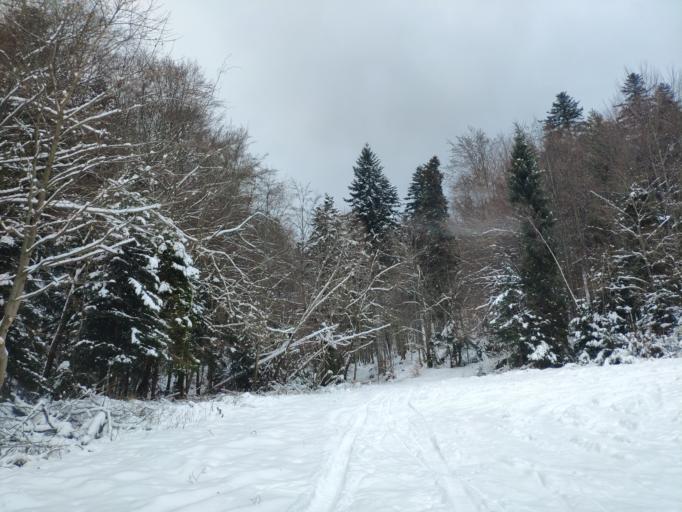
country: SK
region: Kosicky
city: Gelnica
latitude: 48.7662
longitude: 20.9607
